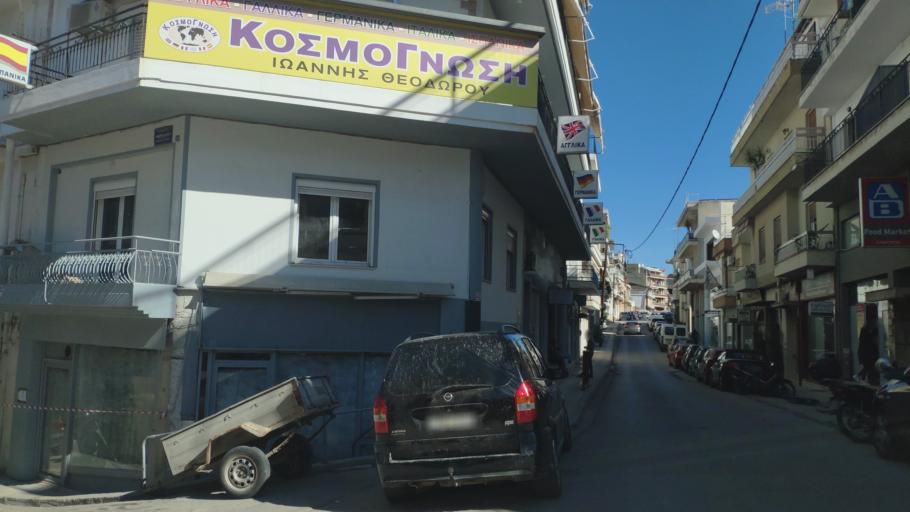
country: GR
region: Central Greece
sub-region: Nomos Voiotias
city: Livadeia
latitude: 38.4374
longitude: 22.8786
